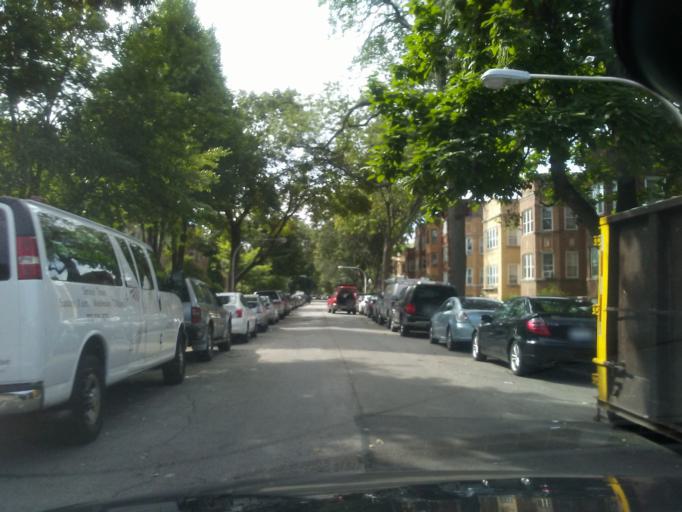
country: US
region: Illinois
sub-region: Cook County
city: Lincolnwood
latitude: 41.9939
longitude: -87.6922
